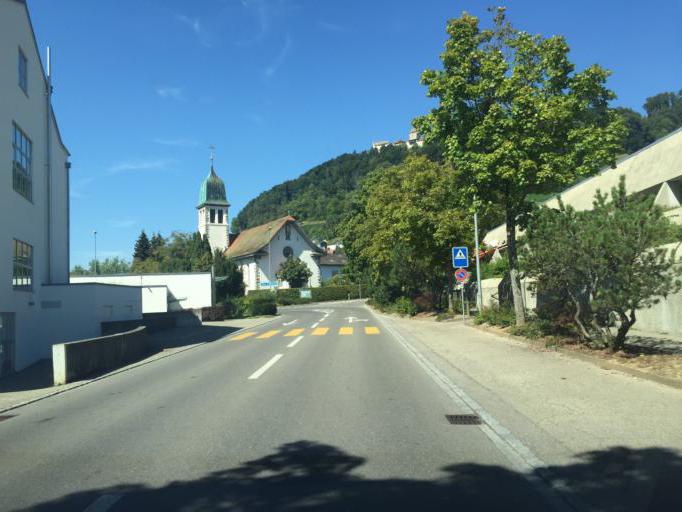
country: CH
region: Schaffhausen
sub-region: Bezirk Stein
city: Stein am Rhein
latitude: 47.6608
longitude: 8.8611
